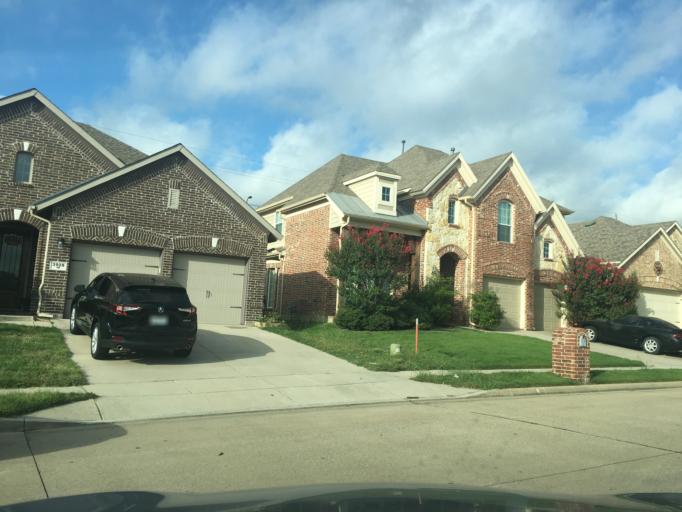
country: US
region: Texas
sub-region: Dallas County
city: Sachse
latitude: 32.9609
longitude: -96.5963
